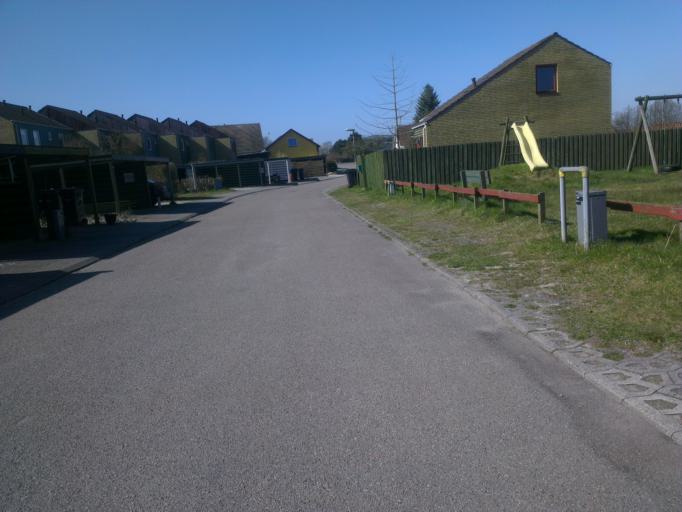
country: DK
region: Capital Region
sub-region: Frederikssund Kommune
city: Frederikssund
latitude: 55.8552
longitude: 12.0661
